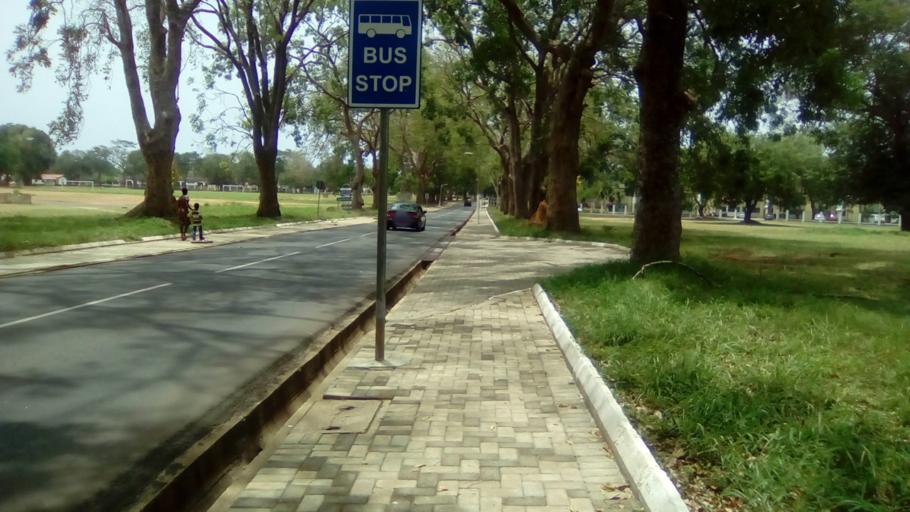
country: GH
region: Greater Accra
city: Medina Estates
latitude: 5.6467
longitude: -0.1891
